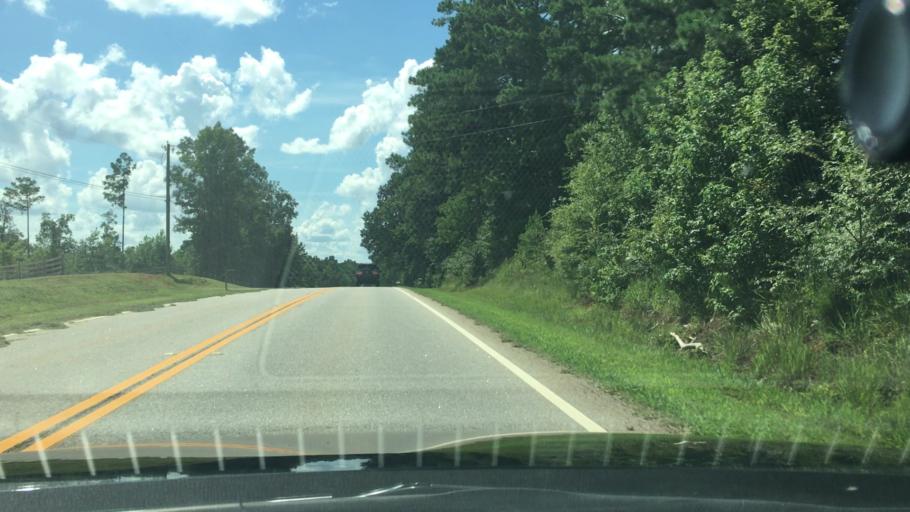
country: US
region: Georgia
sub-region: Putnam County
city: Eatonton
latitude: 33.3082
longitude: -83.5000
